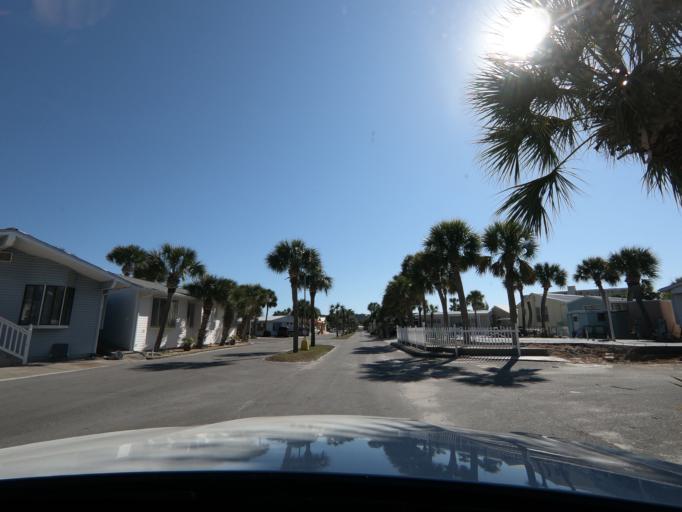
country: US
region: Florida
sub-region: Bay County
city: Lower Grand Lagoon
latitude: 30.1401
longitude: -85.7468
